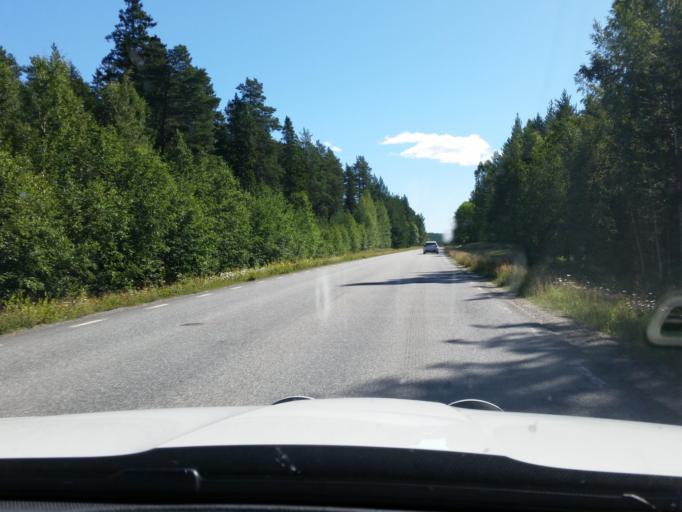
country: SE
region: Norrbotten
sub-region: Pitea Kommun
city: Bergsviken
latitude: 65.3154
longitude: 21.3078
